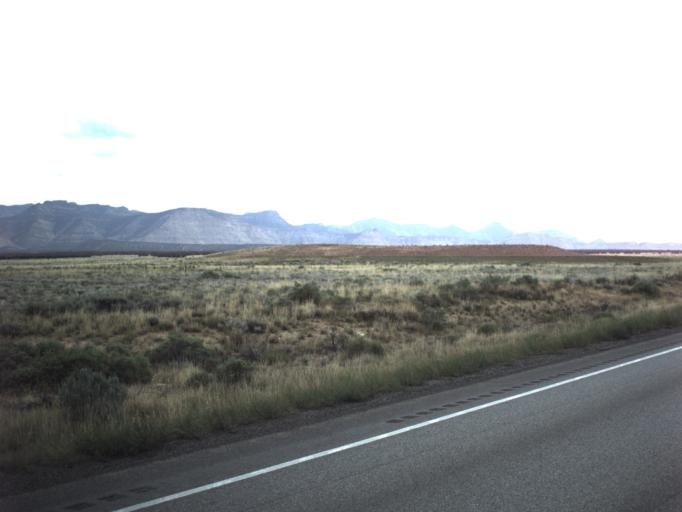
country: US
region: Utah
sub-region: Carbon County
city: East Carbon City
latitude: 39.4420
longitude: -110.4653
